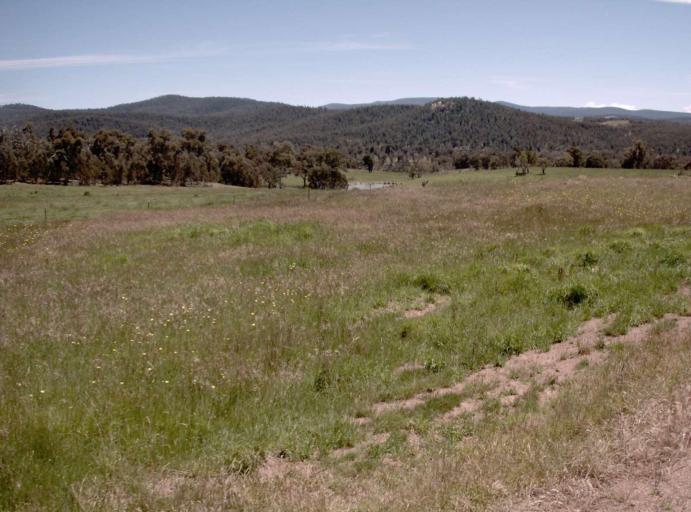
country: AU
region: New South Wales
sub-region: Snowy River
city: Jindabyne
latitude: -37.0830
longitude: 148.2587
